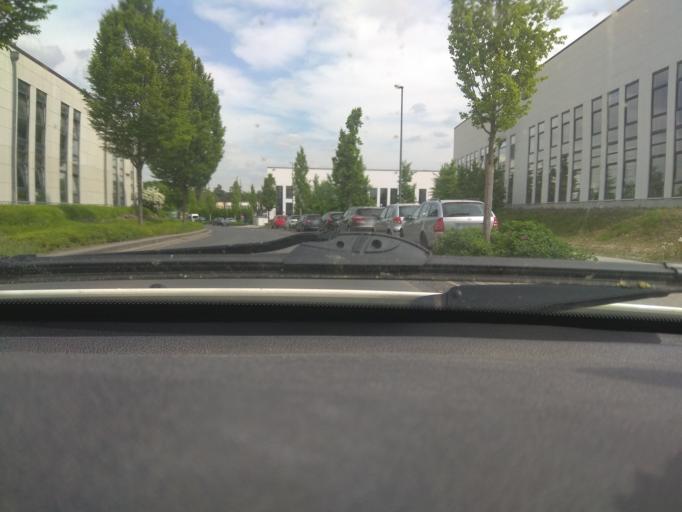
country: DE
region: North Rhine-Westphalia
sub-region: Regierungsbezirk Koln
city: Wahn-Heide
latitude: 50.8409
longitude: 7.1211
